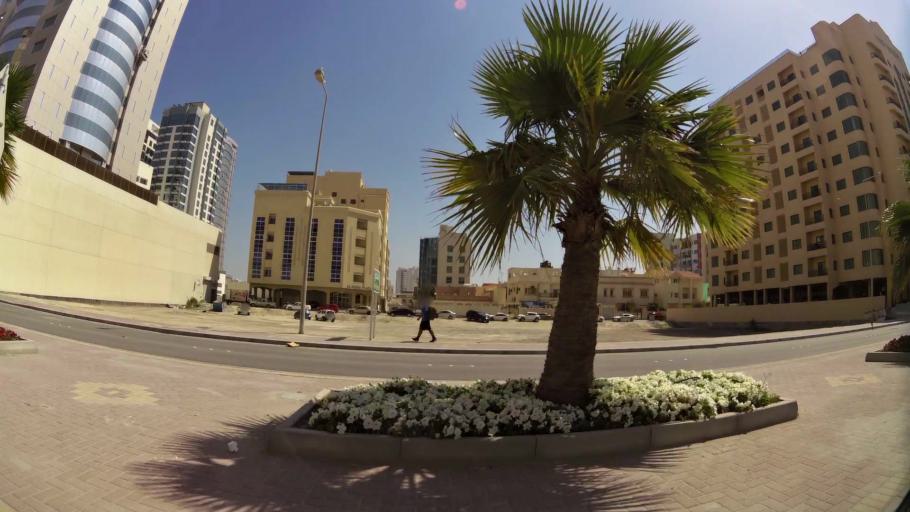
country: BH
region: Manama
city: Manama
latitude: 26.2134
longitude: 50.6099
